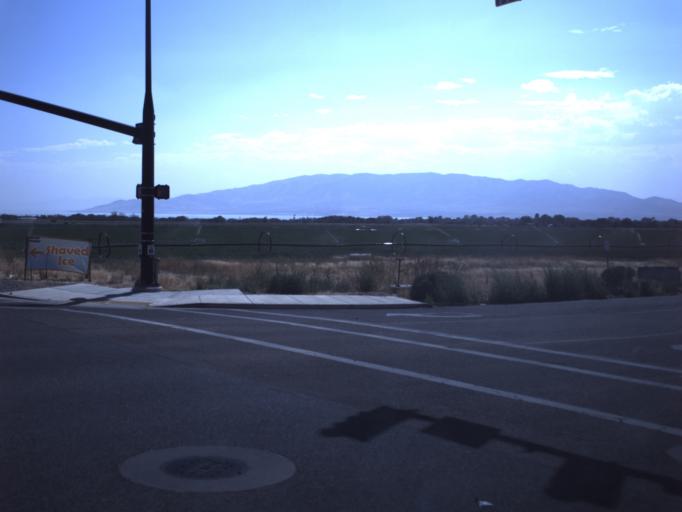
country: US
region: Utah
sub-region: Utah County
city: Cedar Hills
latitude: 40.4156
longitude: -111.7735
